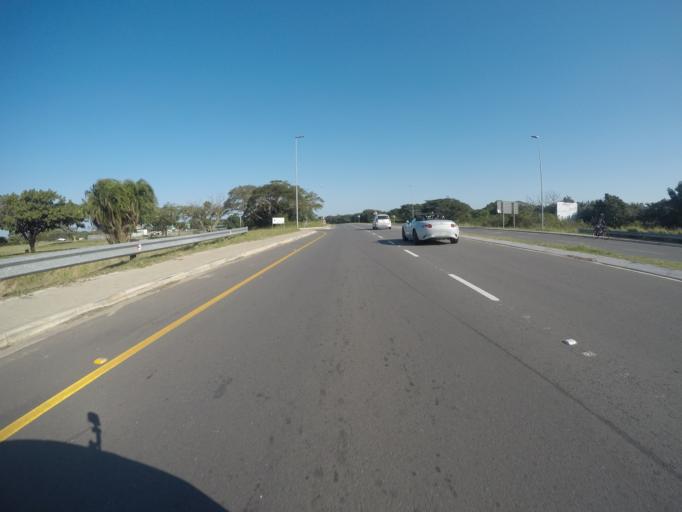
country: ZA
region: KwaZulu-Natal
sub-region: uThungulu District Municipality
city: Richards Bay
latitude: -28.7730
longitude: 32.0682
